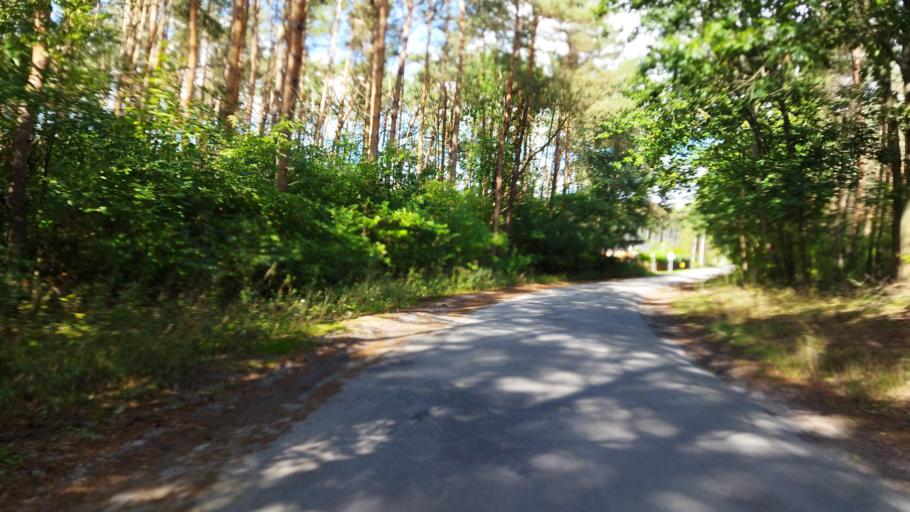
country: DE
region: Lower Saxony
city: Emsburen
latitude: 52.4291
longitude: 7.3400
